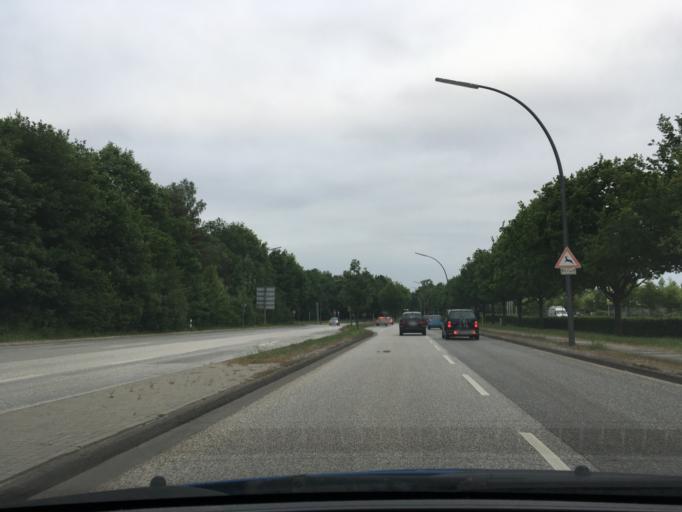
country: DE
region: Lower Saxony
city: Seevetal
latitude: 53.4310
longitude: 9.9327
